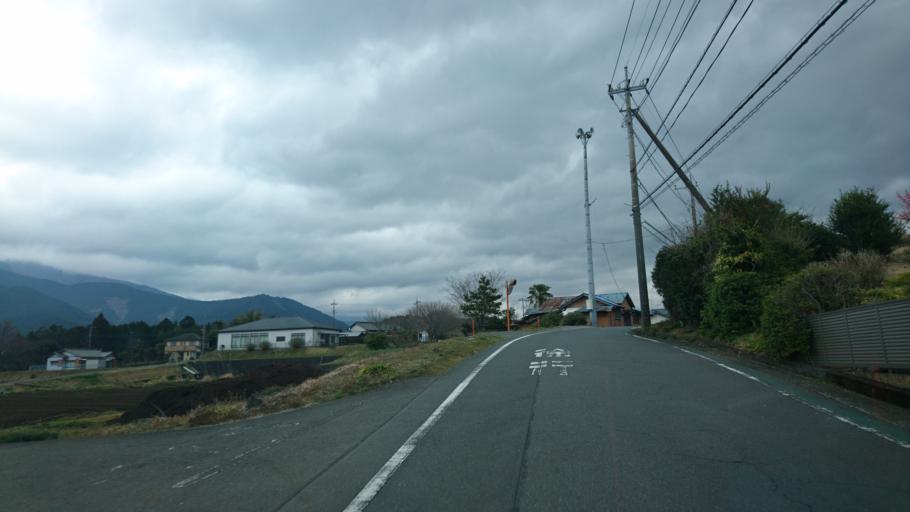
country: JP
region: Shizuoka
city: Fujinomiya
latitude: 35.3081
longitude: 138.5752
